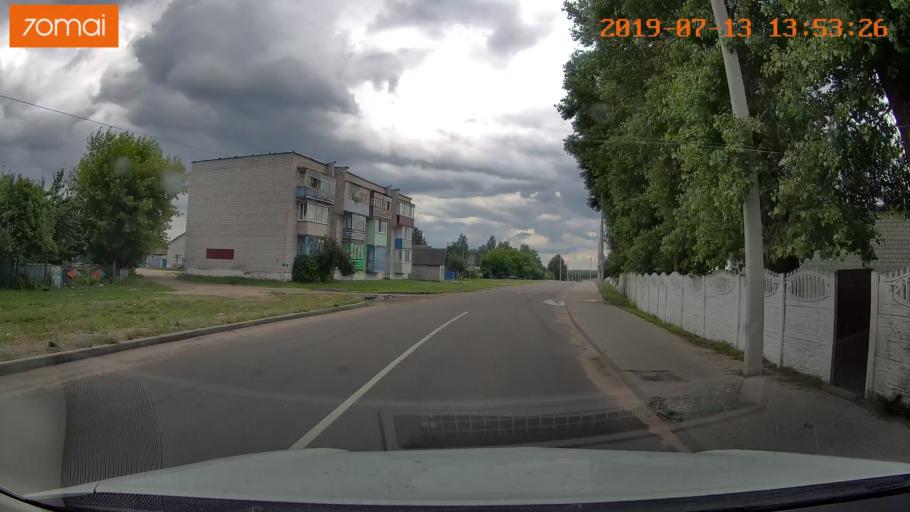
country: BY
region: Mogilev
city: Asipovichy
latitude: 53.2927
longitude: 28.6483
